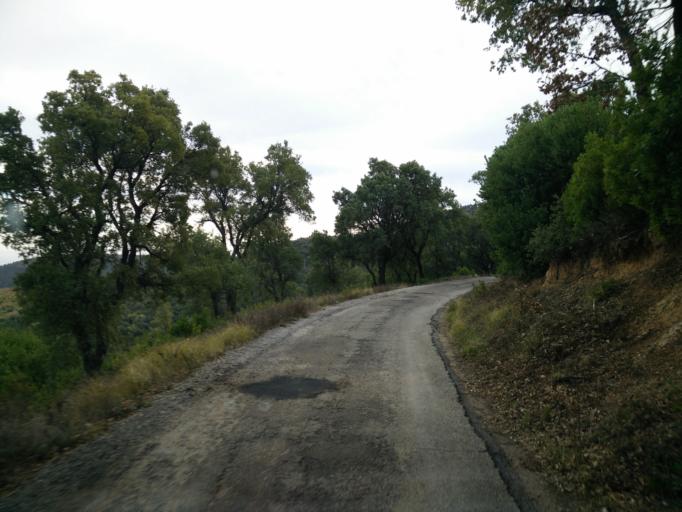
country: FR
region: Provence-Alpes-Cote d'Azur
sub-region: Departement du Var
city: Roquebrune-sur-Argens
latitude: 43.3870
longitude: 6.6150
